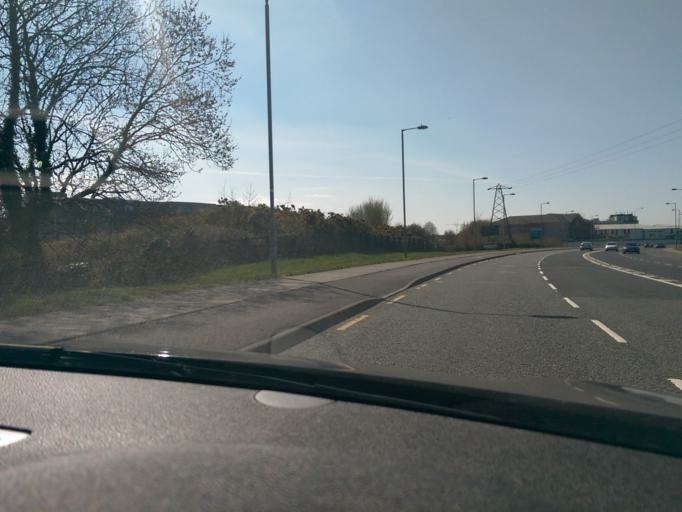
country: IE
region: Connaught
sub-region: County Galway
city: Gaillimh
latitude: 53.2878
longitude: -9.0380
